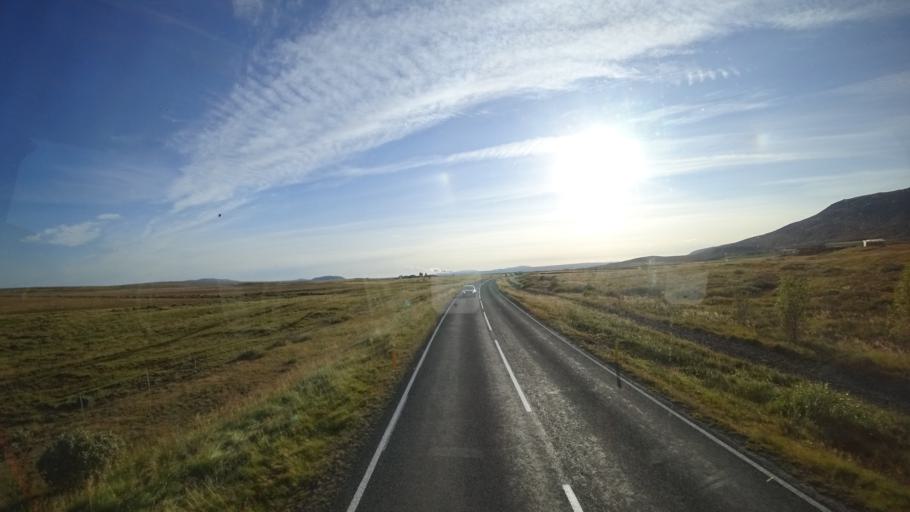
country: IS
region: South
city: Selfoss
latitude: 64.2433
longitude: -20.5033
